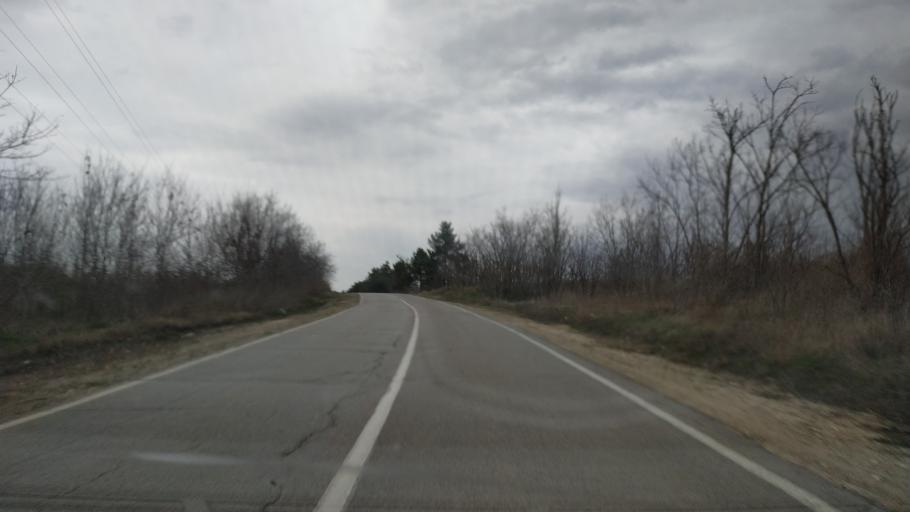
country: RO
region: Vaslui
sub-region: Comuna Vetrisoaia
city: Vetrisoaia
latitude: 46.3925
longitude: 28.2491
